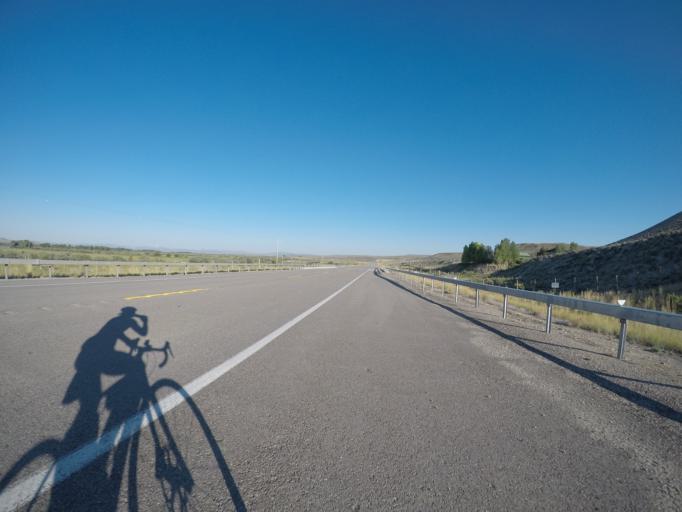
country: US
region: Wyoming
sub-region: Sublette County
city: Pinedale
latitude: 42.8826
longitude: -109.9981
